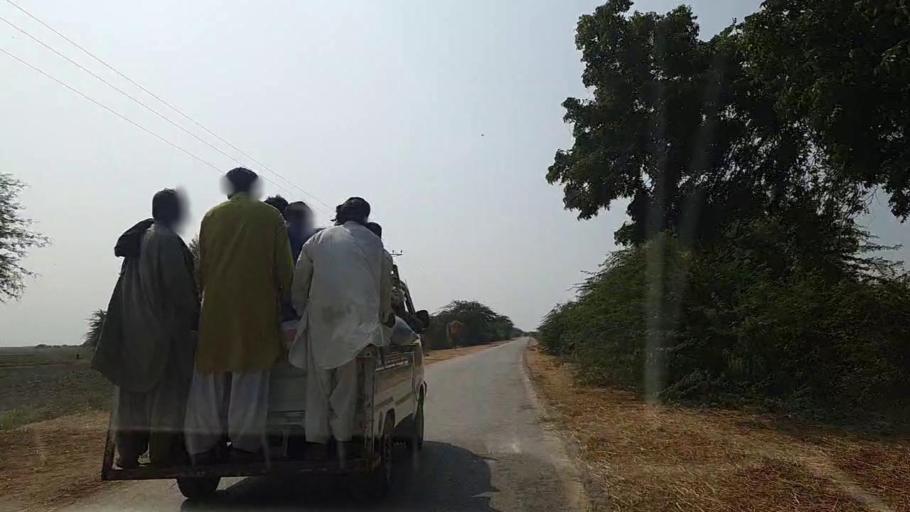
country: PK
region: Sindh
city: Chuhar Jamali
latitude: 24.3670
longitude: 67.9645
